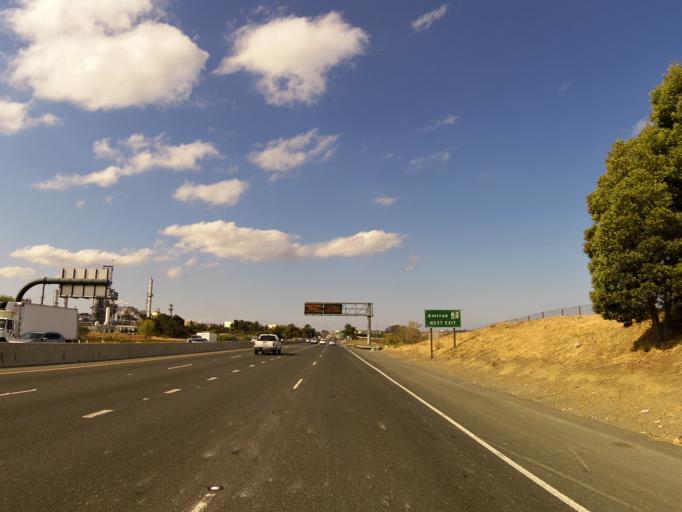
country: US
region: California
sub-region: Contra Costa County
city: Vine Hill
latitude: 38.0207
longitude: -122.1002
